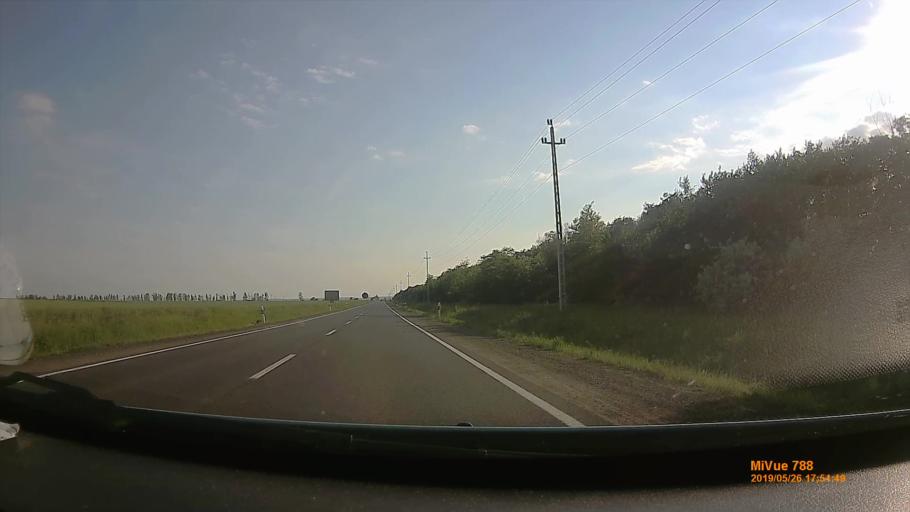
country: HU
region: Borsod-Abauj-Zemplen
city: Arnot
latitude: 48.1364
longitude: 20.8815
